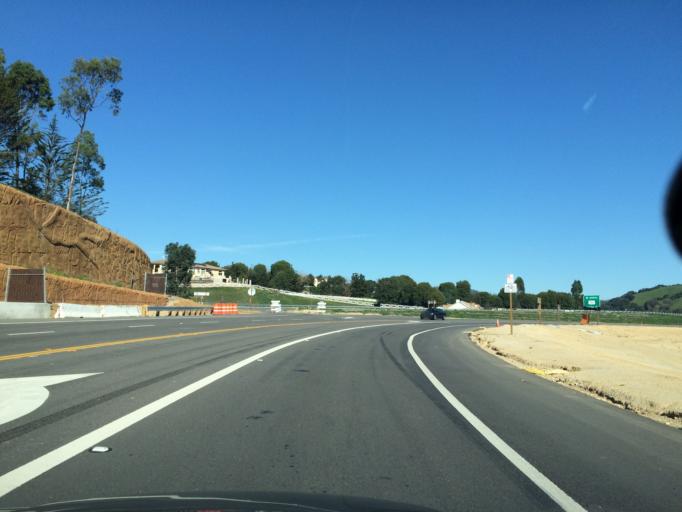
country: US
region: California
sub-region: San Benito County
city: Aromas
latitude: 36.8585
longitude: -121.6305
